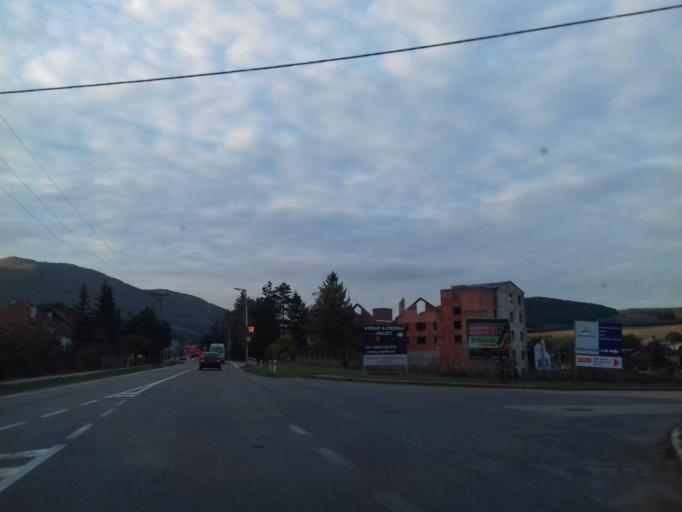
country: SK
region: Trenciansky
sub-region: Okres Trencin
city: Trencin
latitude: 48.8876
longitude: 17.9605
